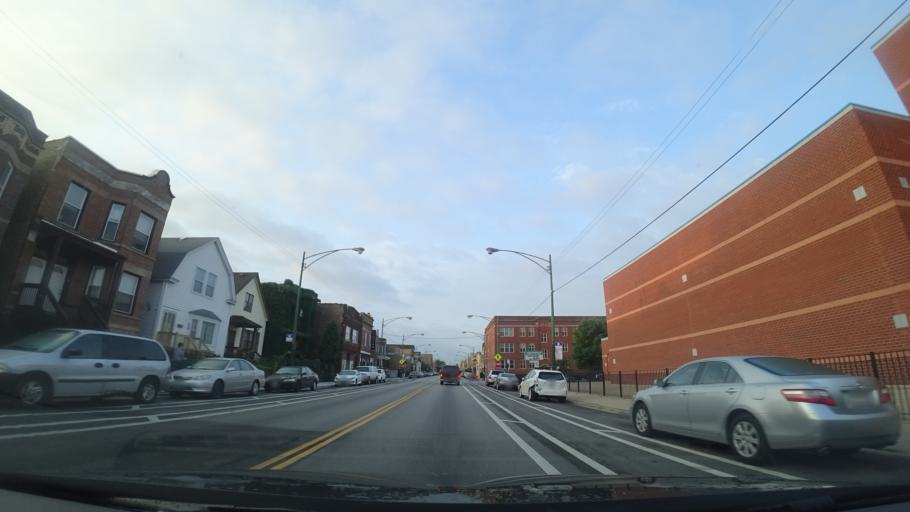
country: US
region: Illinois
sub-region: Cook County
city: Lincolnwood
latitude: 41.9344
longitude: -87.7075
